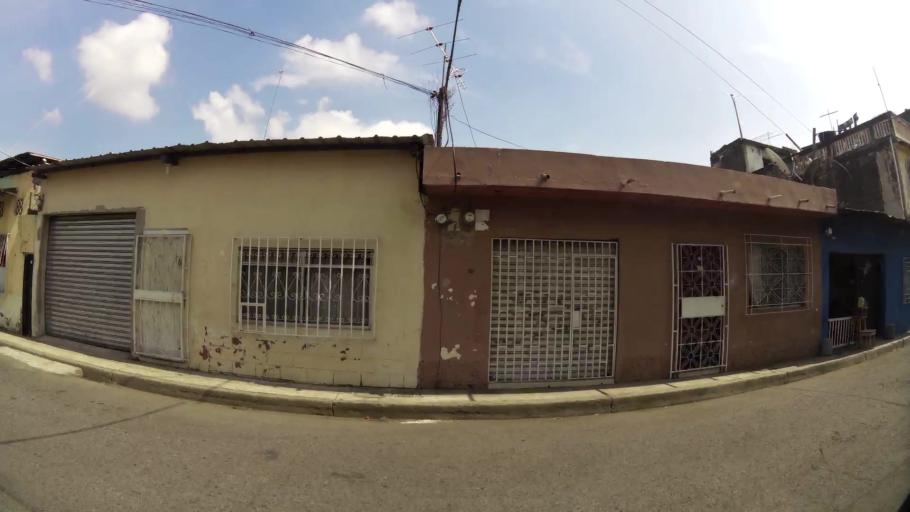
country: EC
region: Guayas
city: Guayaquil
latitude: -2.2599
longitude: -79.8860
